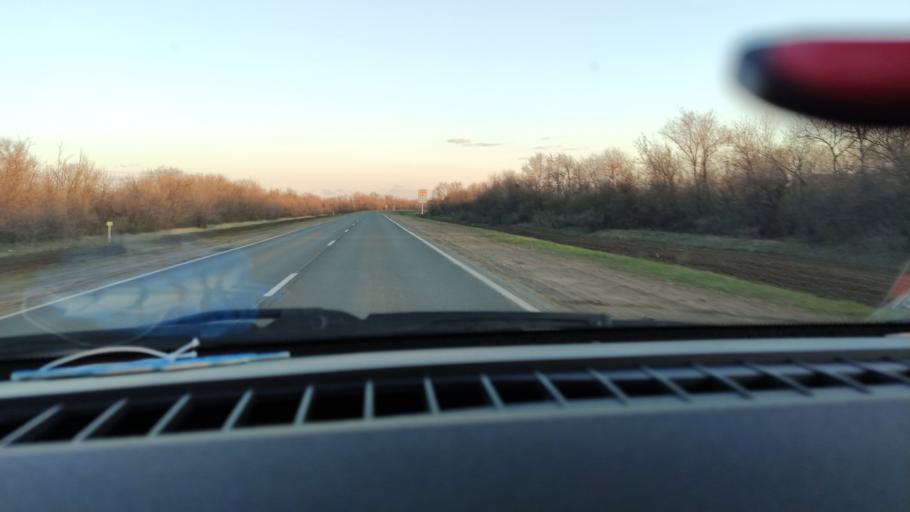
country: RU
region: Saratov
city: Privolzhskiy
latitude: 51.3698
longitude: 46.0466
